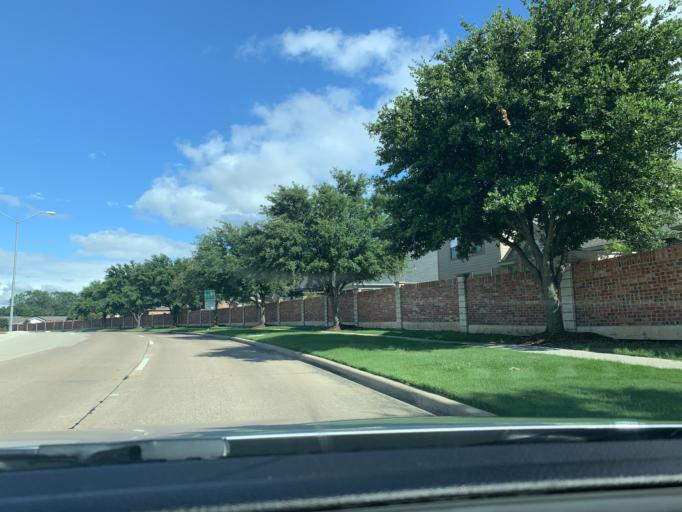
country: US
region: Texas
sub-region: Dallas County
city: Grand Prairie
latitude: 32.6580
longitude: -97.0366
